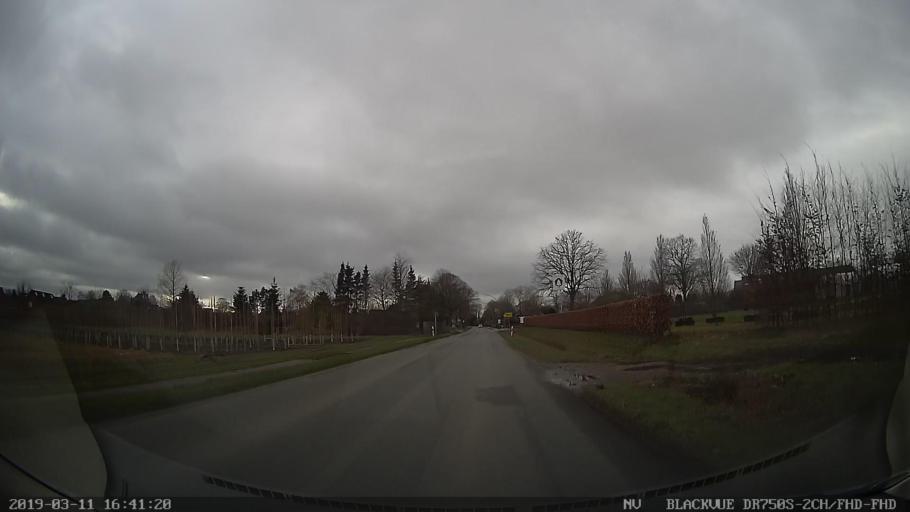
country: DE
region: Schleswig-Holstein
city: Tangstedt
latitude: 53.6616
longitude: 9.8502
